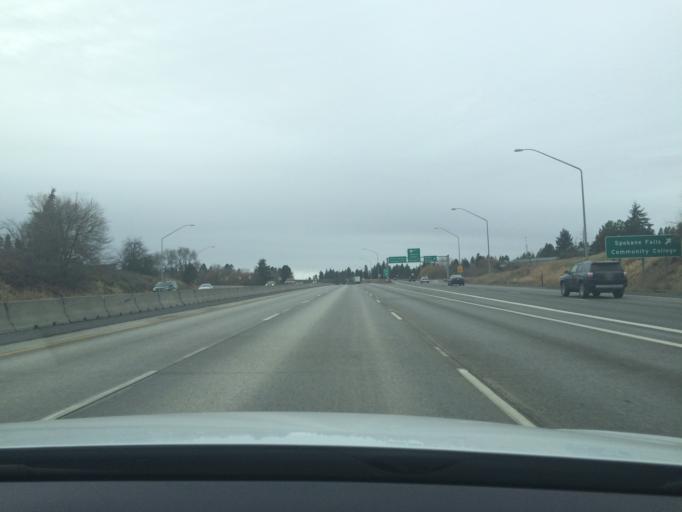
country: US
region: Washington
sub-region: Spokane County
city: Spokane
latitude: 47.6373
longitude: -117.4727
